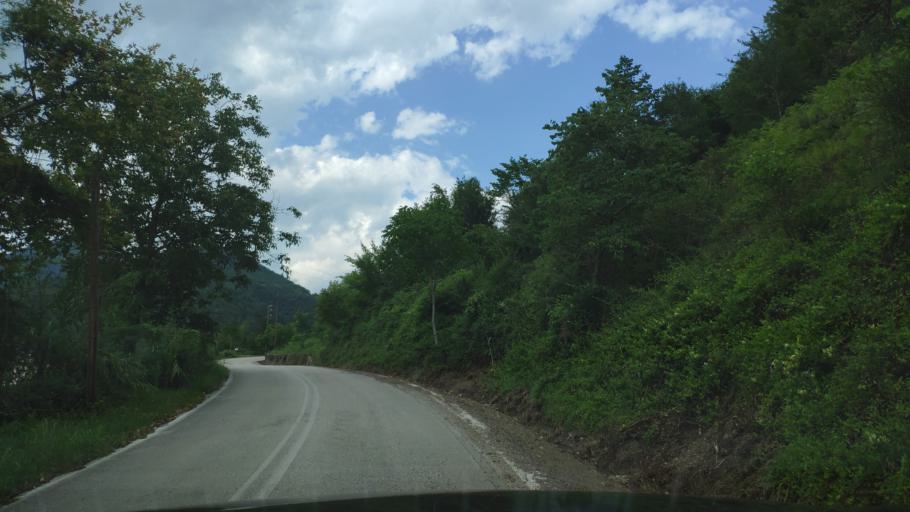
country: GR
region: Epirus
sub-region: Nomos Artas
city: Agios Dimitrios
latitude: 39.4569
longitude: 21.0348
